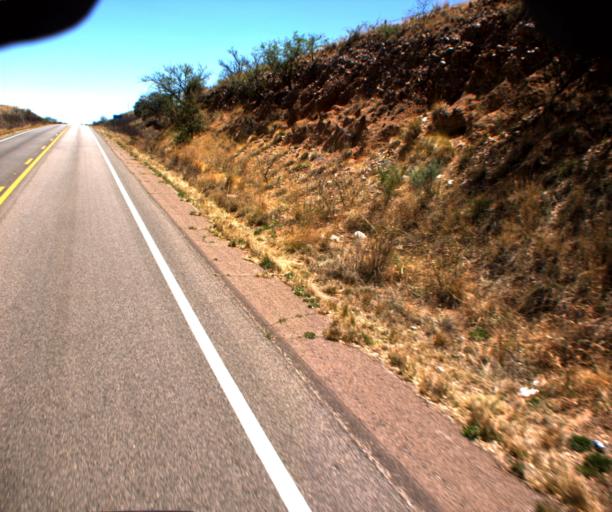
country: US
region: Arizona
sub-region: Pima County
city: Corona de Tucson
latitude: 31.7348
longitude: -110.6617
